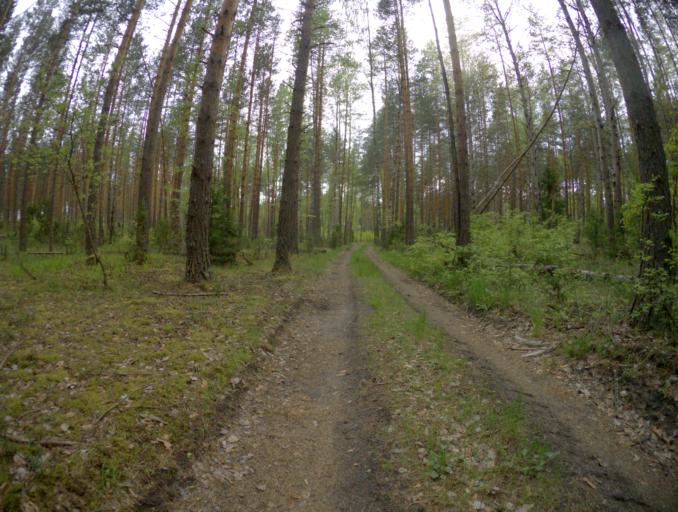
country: RU
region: Rjazan
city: Gus'-Zheleznyy
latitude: 55.1261
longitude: 41.1445
